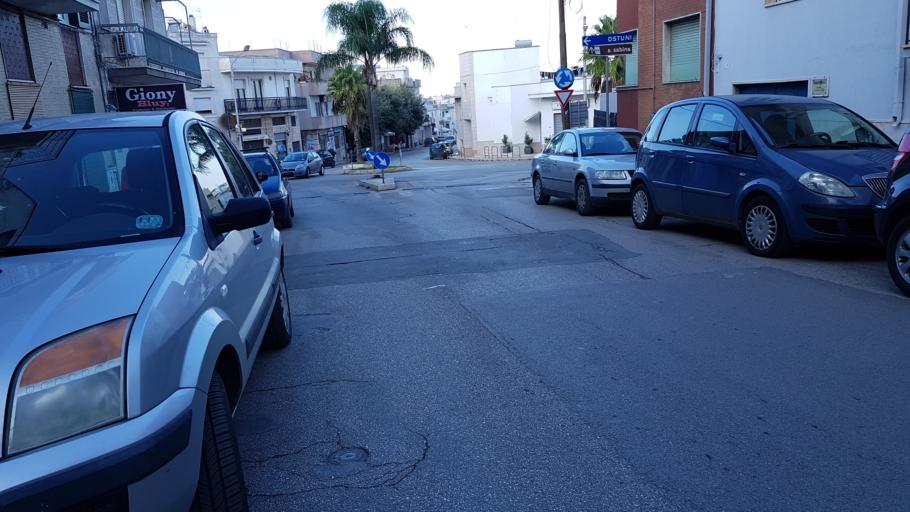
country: IT
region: Apulia
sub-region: Provincia di Brindisi
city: Carovigno
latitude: 40.7099
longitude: 17.6589
